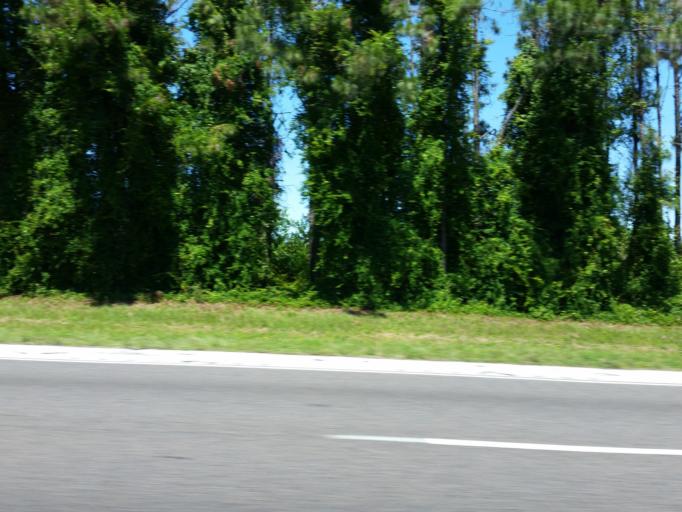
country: US
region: Florida
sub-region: Hillsborough County
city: Ruskin
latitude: 27.6555
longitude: -82.4389
